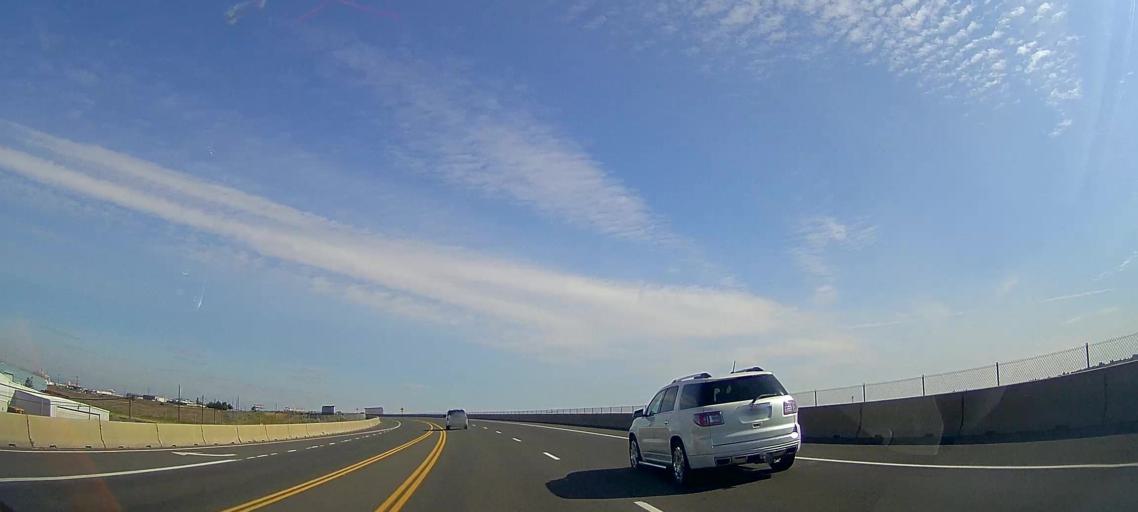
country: US
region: Oregon
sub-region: Jefferson County
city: Madras
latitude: 44.6537
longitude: -121.1289
